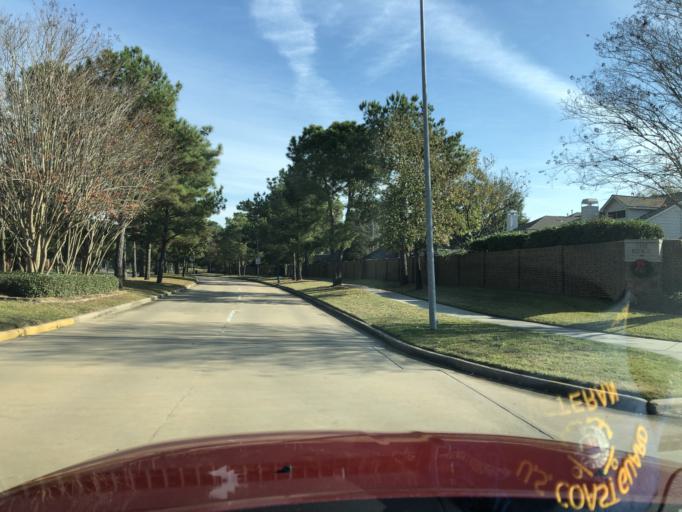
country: US
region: Texas
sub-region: Harris County
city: Tomball
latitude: 30.0338
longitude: -95.5652
